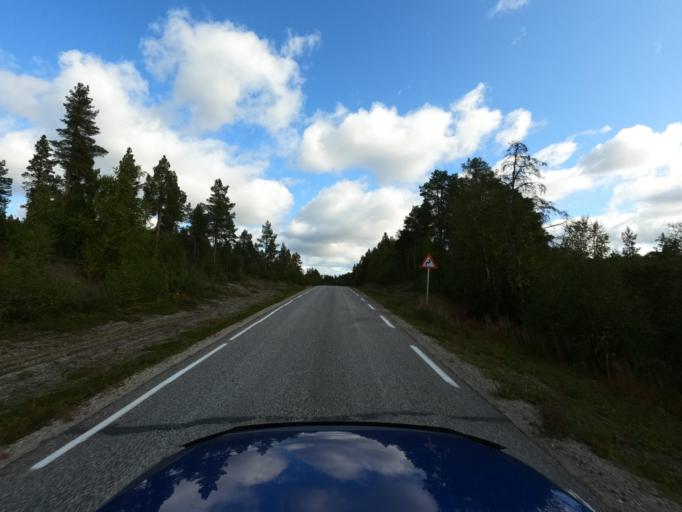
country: NO
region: Finnmark Fylke
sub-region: Karasjok
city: Karasjohka
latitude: 69.4355
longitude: 25.1574
